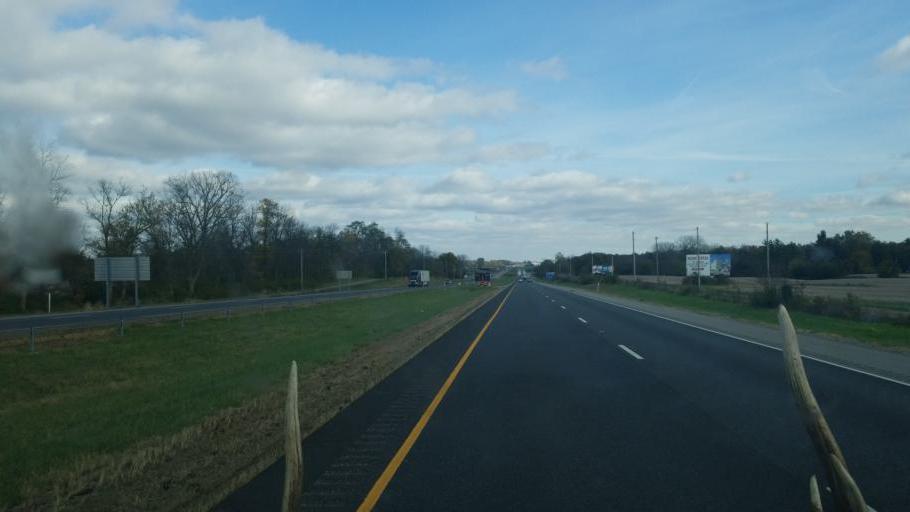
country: US
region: Indiana
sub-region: Wayne County
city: Centerville
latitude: 39.8594
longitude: -85.0086
